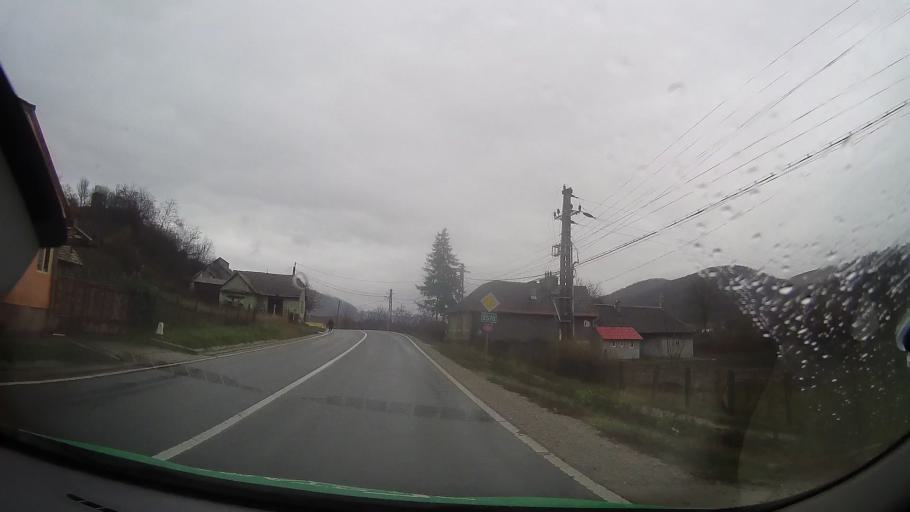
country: RO
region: Bistrita-Nasaud
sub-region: Comuna Galatii Bistritei
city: Galatii Bistritei
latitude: 46.9472
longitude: 24.4559
